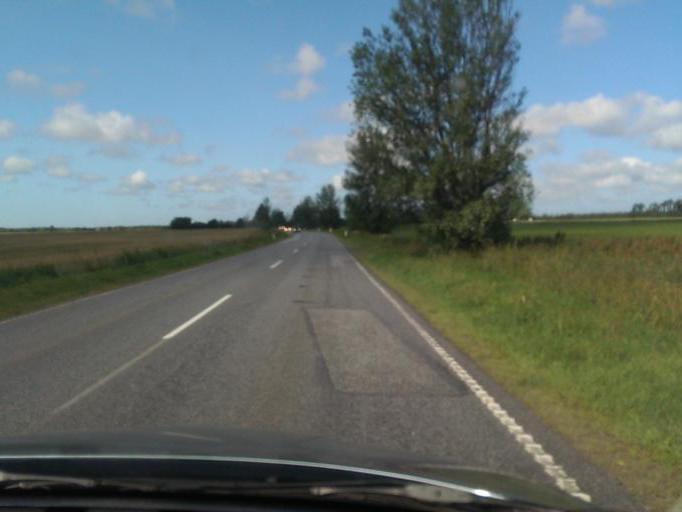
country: DK
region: North Denmark
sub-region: Bronderslev Kommune
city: Bronderslev
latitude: 57.2097
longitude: 9.9083
